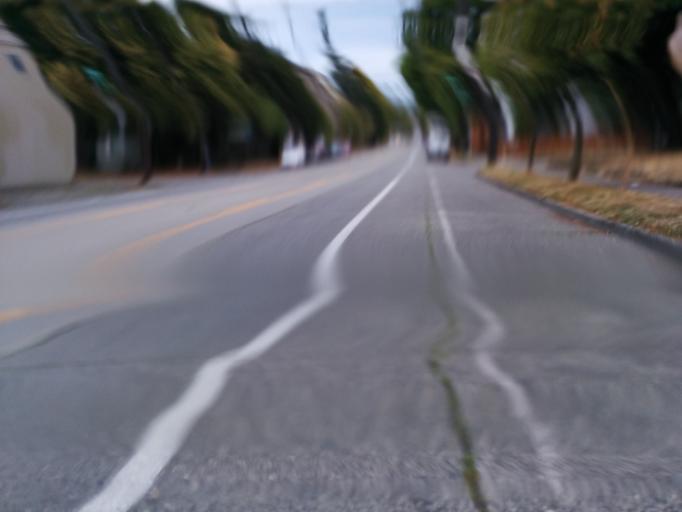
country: US
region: Washington
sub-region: King County
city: Seattle
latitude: 47.6640
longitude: -122.3662
